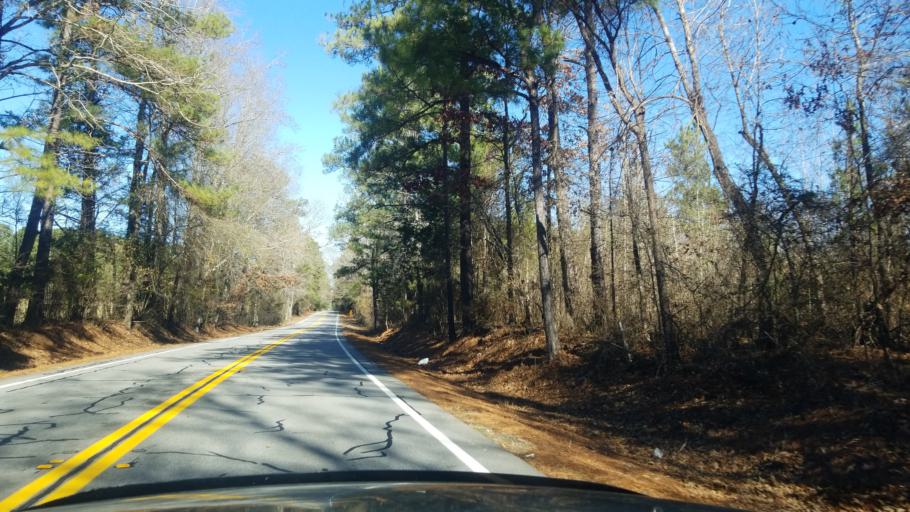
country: US
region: Georgia
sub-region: Harris County
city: Hamilton
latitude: 32.6770
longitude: -84.8591
